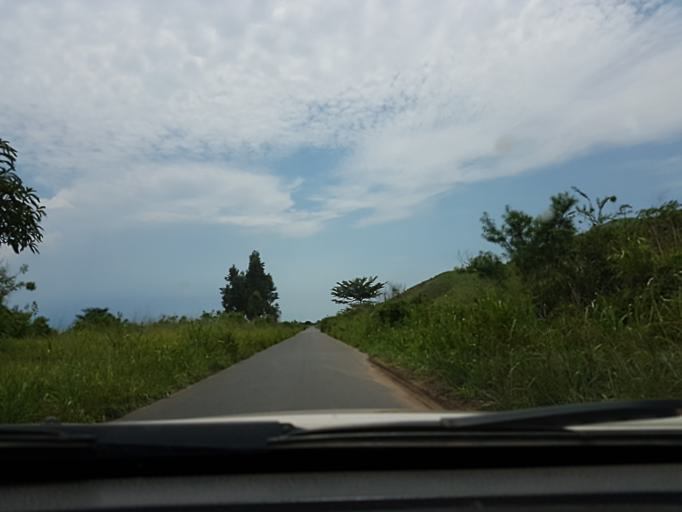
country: CD
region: South Kivu
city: Uvira
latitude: -3.2606
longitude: 29.1612
